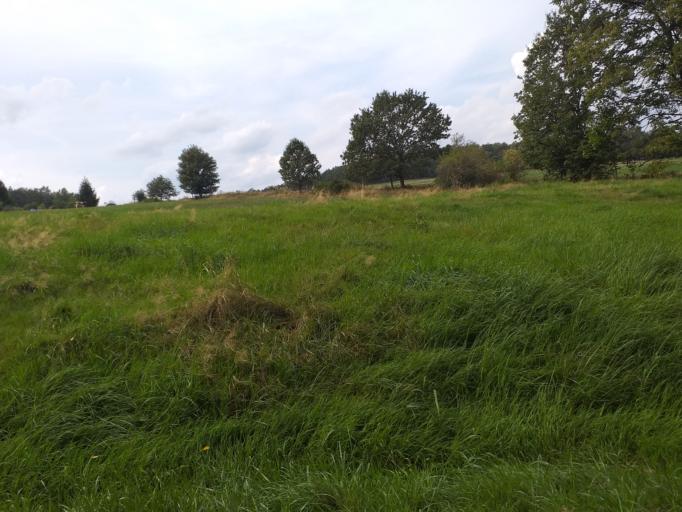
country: PL
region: Lower Silesian Voivodeship
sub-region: Powiat lubanski
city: Lesna
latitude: 51.0021
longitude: 15.3158
